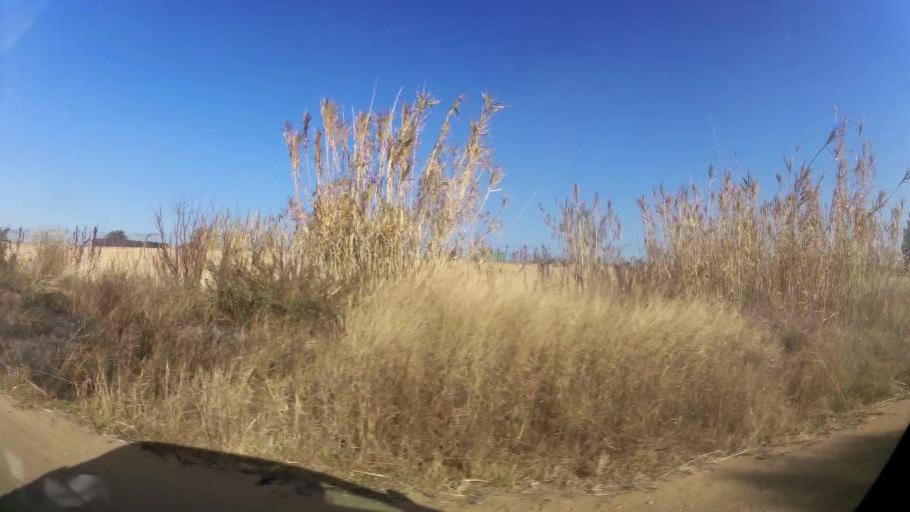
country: ZA
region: Gauteng
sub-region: West Rand District Municipality
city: Muldersdriseloop
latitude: -26.0235
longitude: 27.8738
